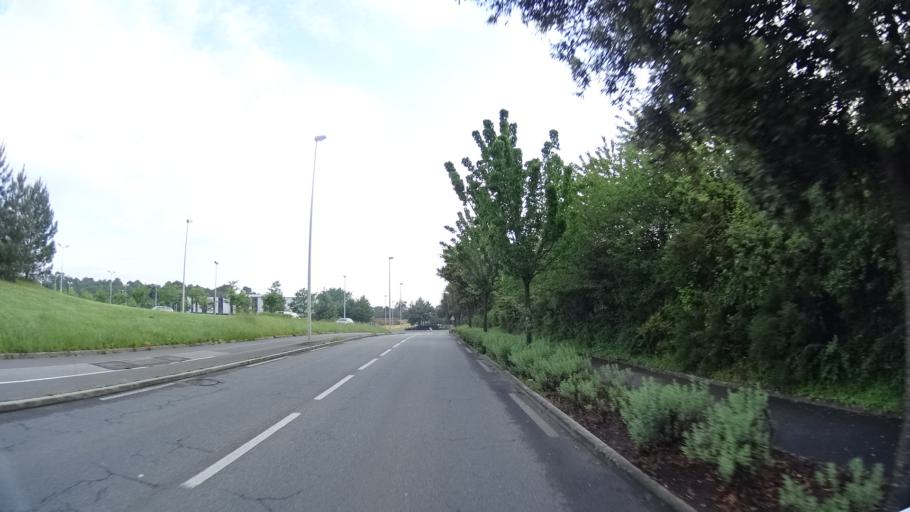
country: FR
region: Brittany
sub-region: Departement du Morbihan
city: Vannes
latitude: 47.6451
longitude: -2.7438
